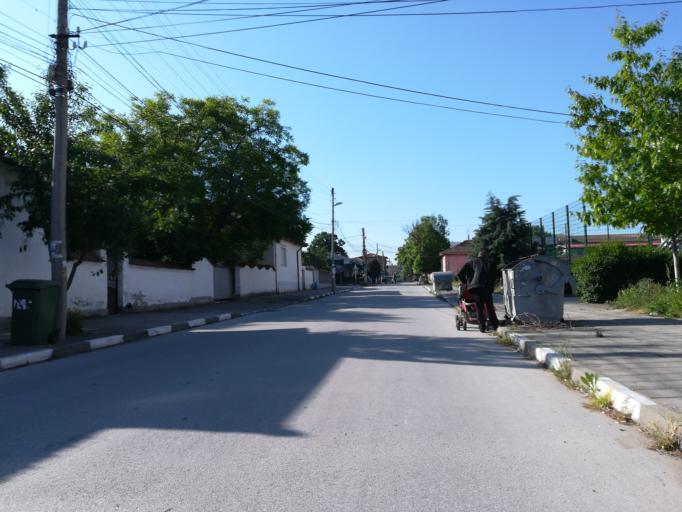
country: BG
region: Stara Zagora
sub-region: Obshtina Chirpan
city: Chirpan
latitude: 42.1034
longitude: 25.2253
